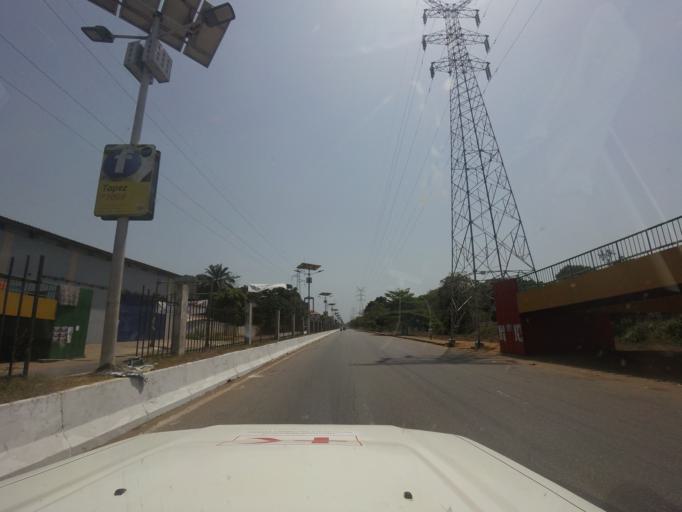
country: GN
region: Conakry
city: Camayenne
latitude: 9.5324
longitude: -13.6828
